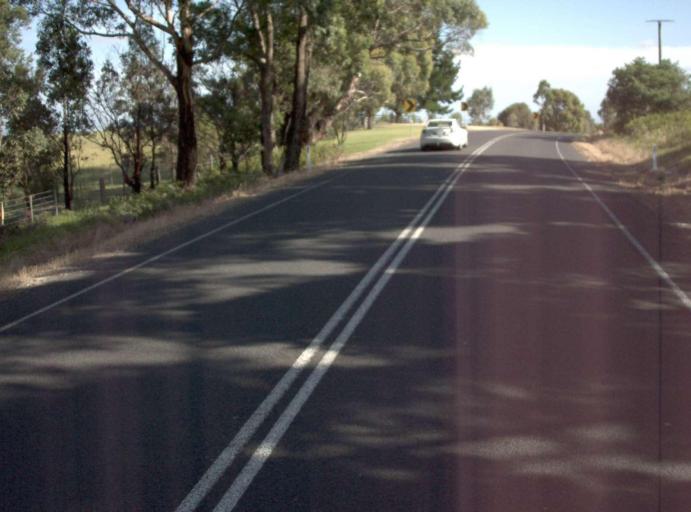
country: AU
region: Victoria
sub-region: East Gippsland
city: Lakes Entrance
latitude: -37.8709
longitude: 147.8476
